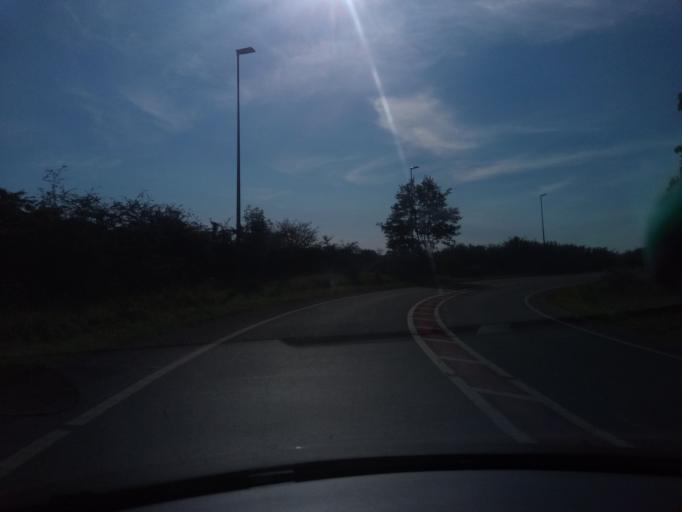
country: GB
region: England
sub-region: Stockton-on-Tees
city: Yarm
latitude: 54.4711
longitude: -1.3230
